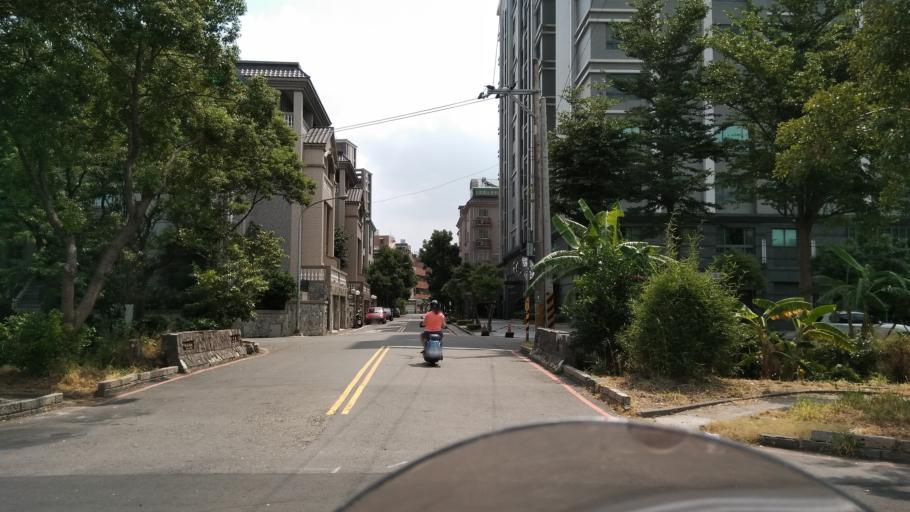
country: TW
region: Taiwan
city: Taoyuan City
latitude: 25.0217
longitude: 121.2641
